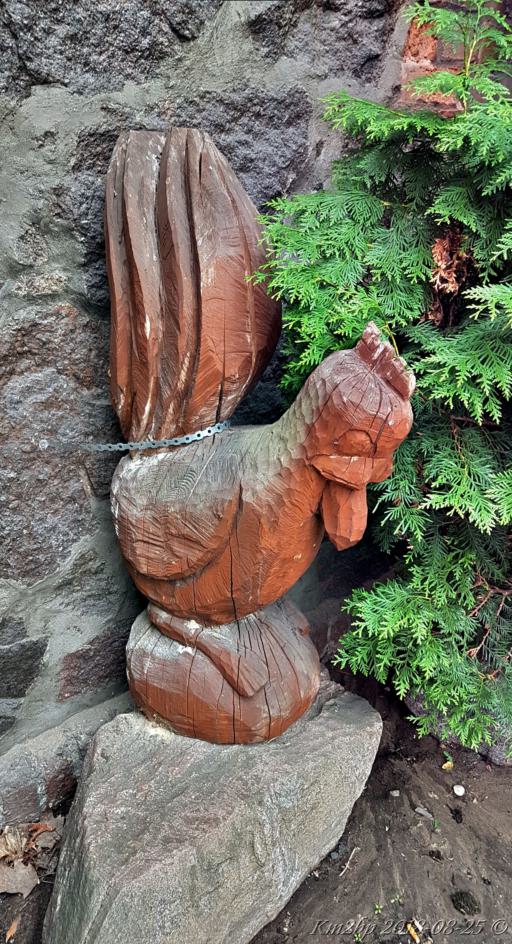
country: PL
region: Lubusz
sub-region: Powiat zielonogorski
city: Zabor
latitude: 51.9575
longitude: 15.6261
